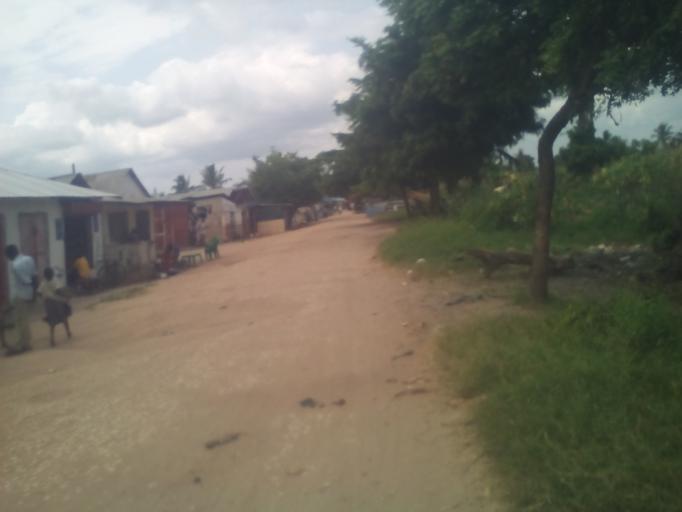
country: TZ
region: Dar es Salaam
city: Dar es Salaam
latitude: -6.8662
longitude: 39.2384
